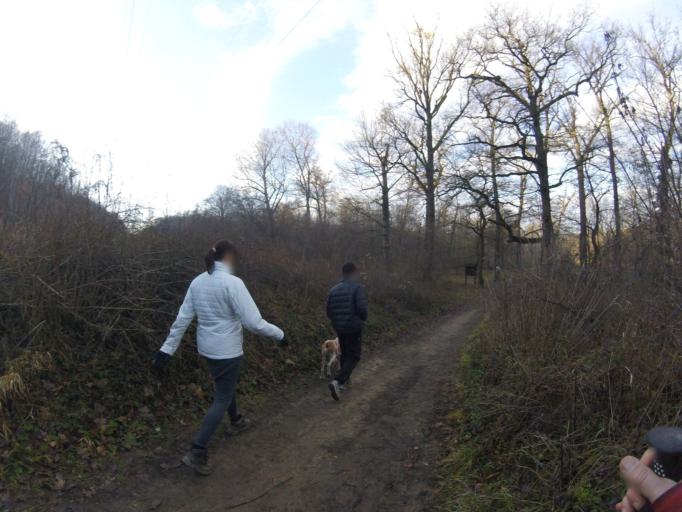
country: HU
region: Pest
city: Budakeszi
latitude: 47.5397
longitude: 18.9553
